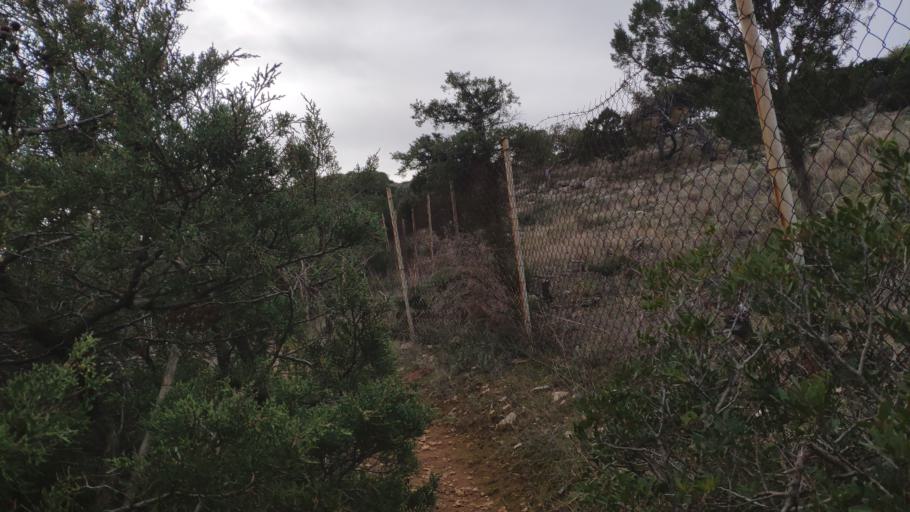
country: GR
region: Attica
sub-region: Nomarchia Anatolikis Attikis
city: Limin Mesoyaias
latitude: 37.9089
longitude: 24.0393
